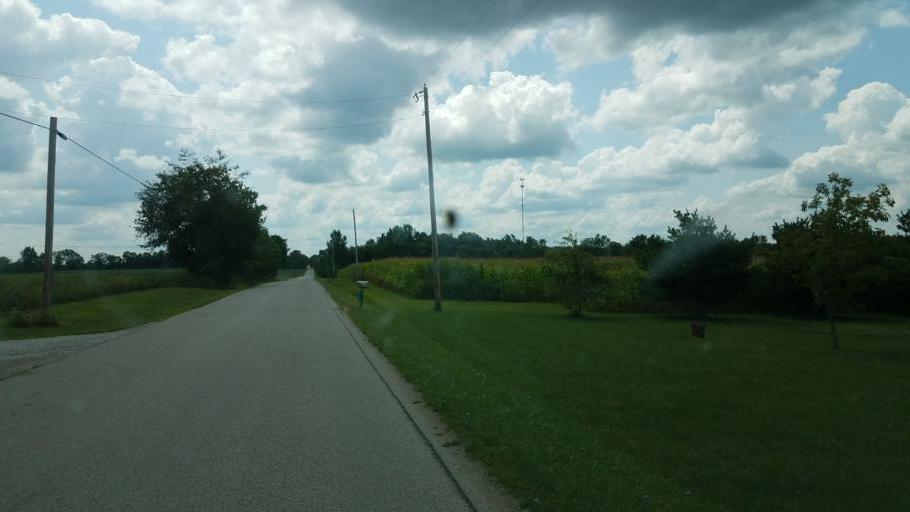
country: US
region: Ohio
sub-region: Morrow County
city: Cardington
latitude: 40.4266
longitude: -82.8090
